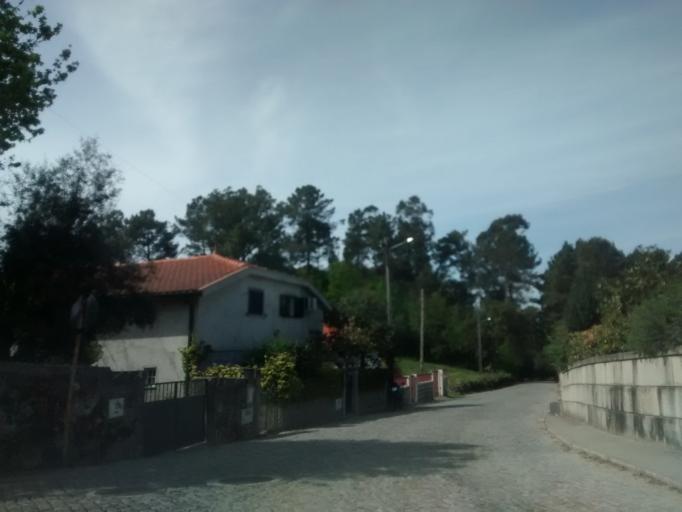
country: PT
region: Braga
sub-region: Braga
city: Braga
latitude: 41.5442
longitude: -8.4429
